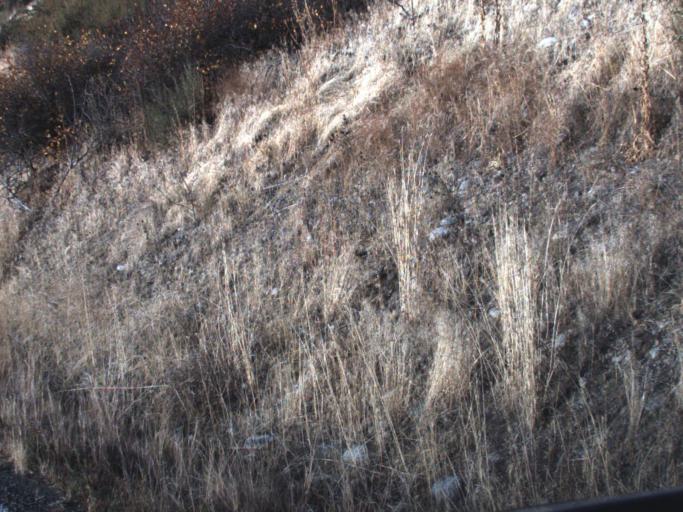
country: US
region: Washington
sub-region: Okanogan County
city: Coulee Dam
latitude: 47.9795
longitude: -118.6960
